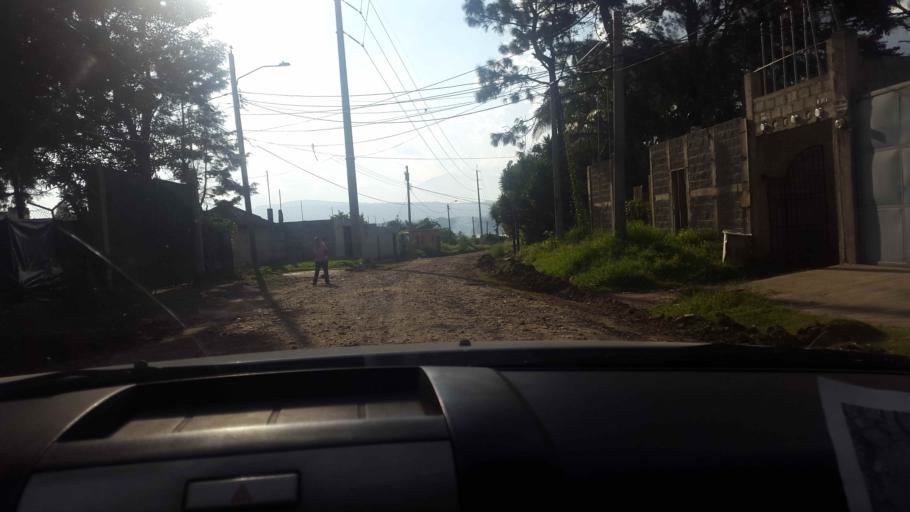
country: GT
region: Guatemala
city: Petapa
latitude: 14.5147
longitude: -90.5449
